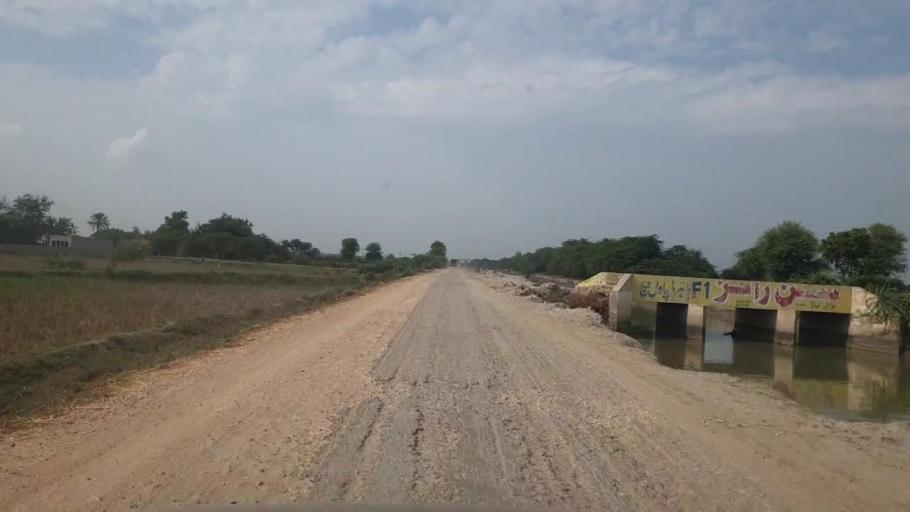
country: PK
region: Sindh
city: Kario
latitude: 24.6339
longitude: 68.5685
